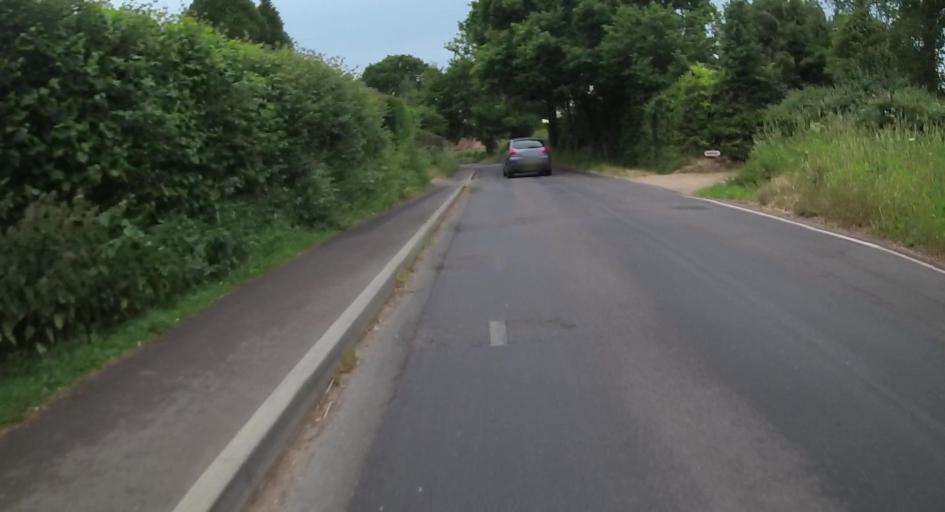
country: GB
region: England
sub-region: Hampshire
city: Fleet
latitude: 51.2687
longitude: -0.8680
